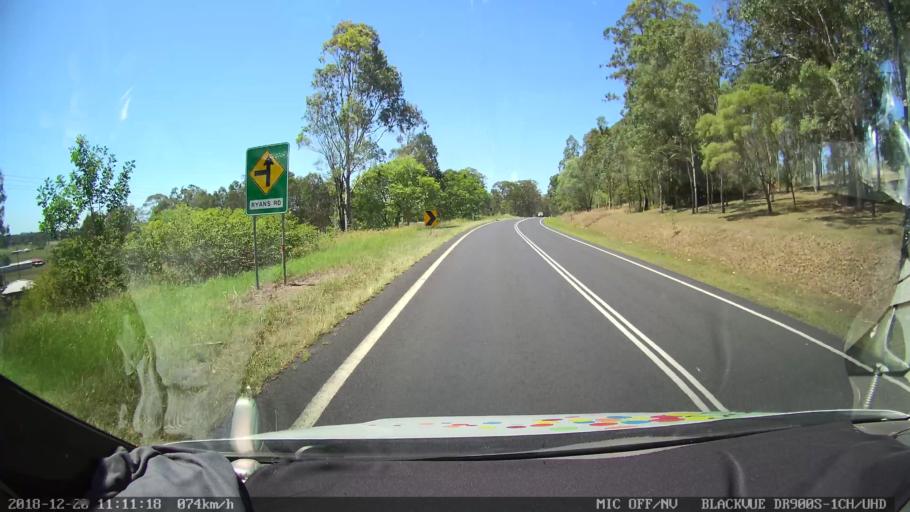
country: AU
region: New South Wales
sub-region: Richmond Valley
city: Casino
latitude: -28.9593
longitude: 153.0136
